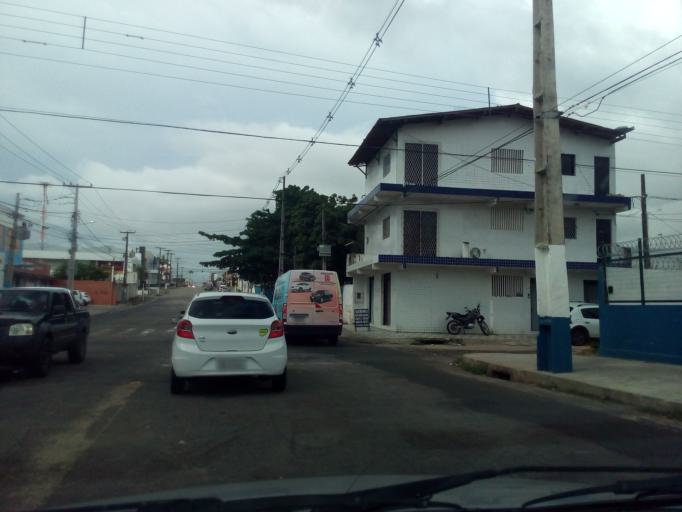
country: BR
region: Rio Grande do Norte
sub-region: Natal
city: Natal
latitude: -5.8122
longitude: -35.2125
